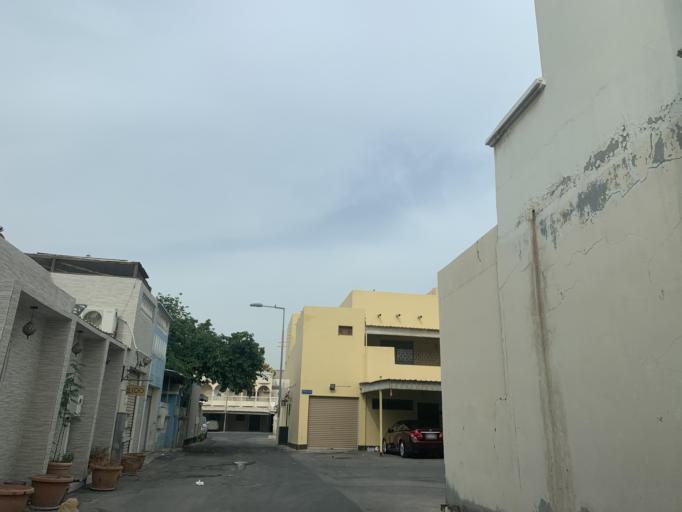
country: BH
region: Northern
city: Madinat `Isa
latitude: 26.1776
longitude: 50.5472
